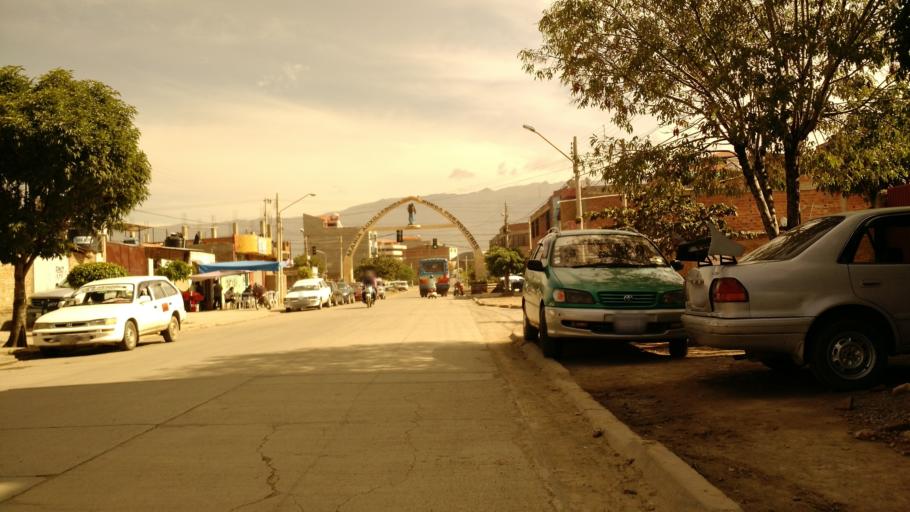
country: BO
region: Cochabamba
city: Cochabamba
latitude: -17.4301
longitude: -66.1588
